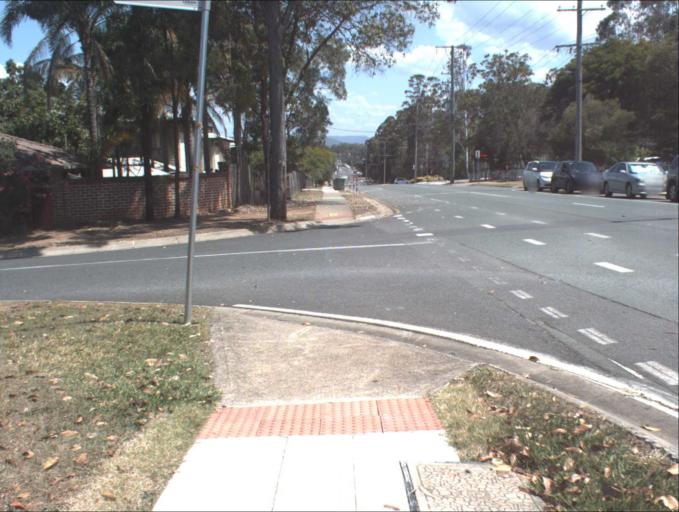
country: AU
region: Queensland
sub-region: Logan
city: Beenleigh
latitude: -27.6917
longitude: 153.2151
